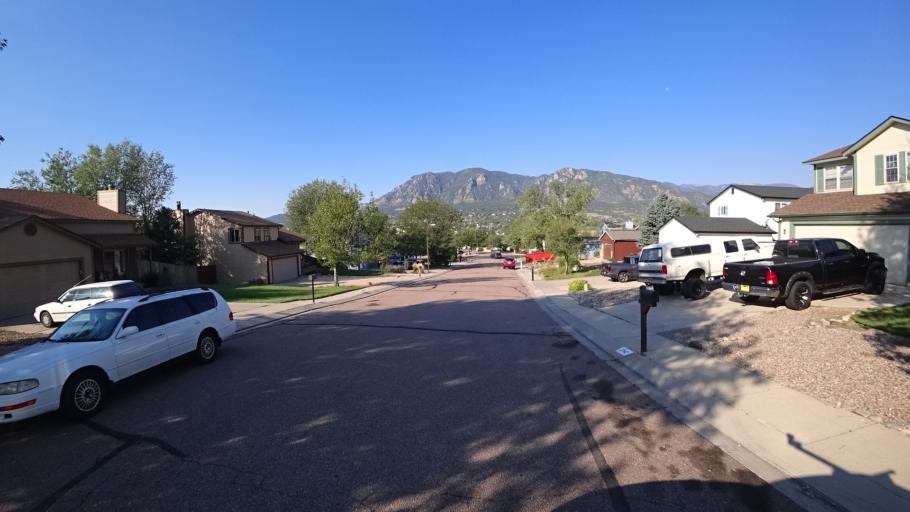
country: US
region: Colorado
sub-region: El Paso County
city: Stratmoor
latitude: 38.7770
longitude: -104.8024
